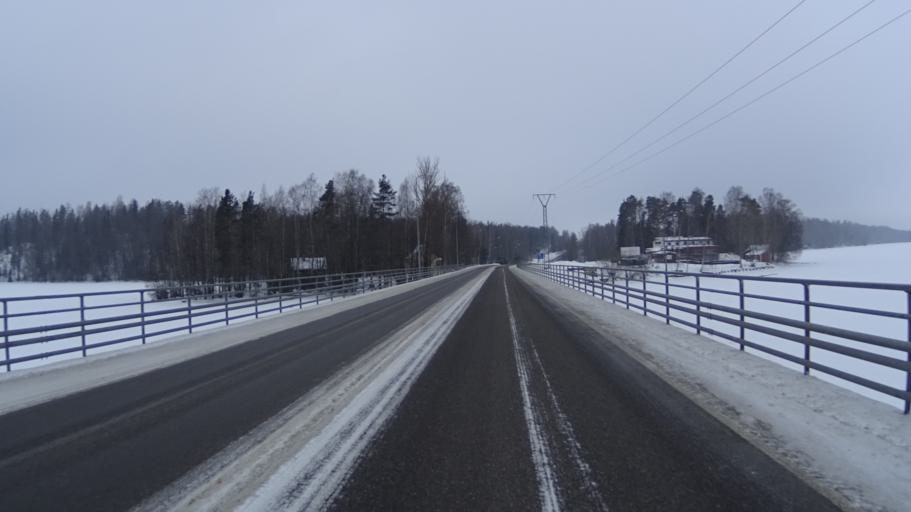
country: FI
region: Uusimaa
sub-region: Helsinki
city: Lohja
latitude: 60.3618
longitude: 24.1705
